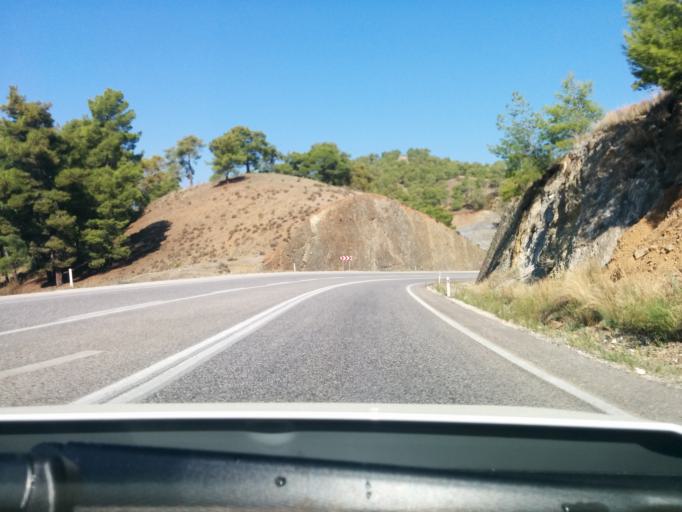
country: TR
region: Mugla
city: Kemer
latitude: 36.6200
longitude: 29.3521
